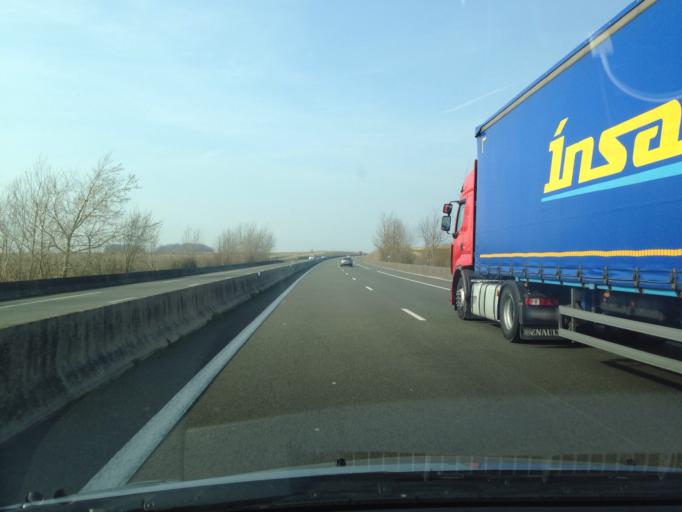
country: FR
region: Picardie
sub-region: Departement de la Somme
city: Nouvion
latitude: 50.2139
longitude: 1.7538
